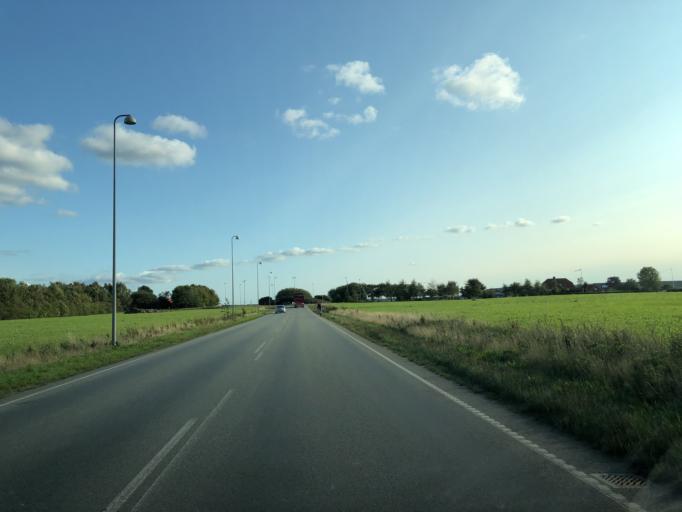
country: DK
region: Central Jutland
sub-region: Viborg Kommune
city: Viborg
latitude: 56.4512
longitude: 9.3430
